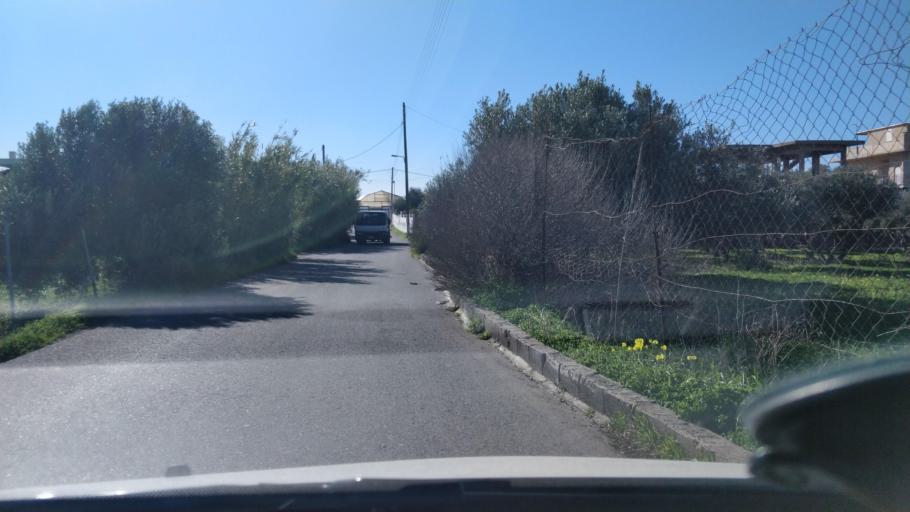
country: GR
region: Crete
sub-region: Nomos Lasithiou
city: Gra Liyia
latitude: 35.0144
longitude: 25.6770
